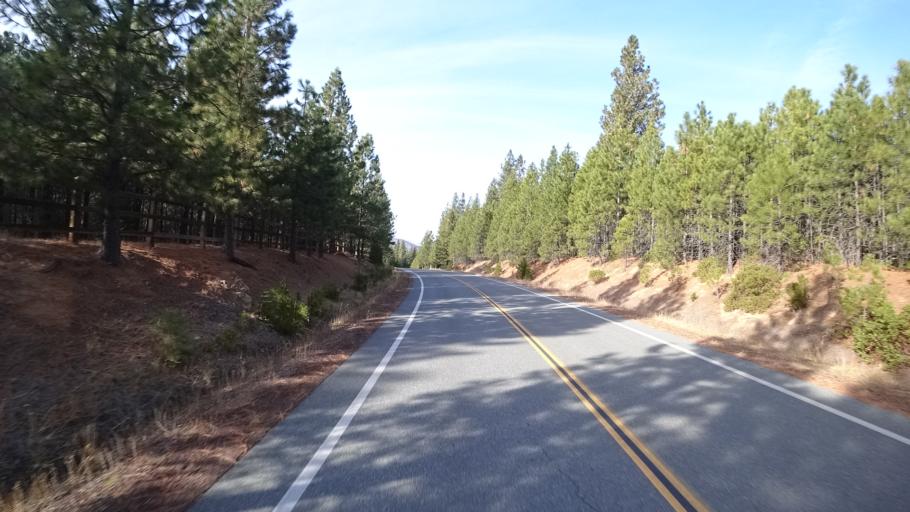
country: US
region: California
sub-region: Siskiyou County
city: Weed
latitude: 41.3897
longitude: -122.4103
